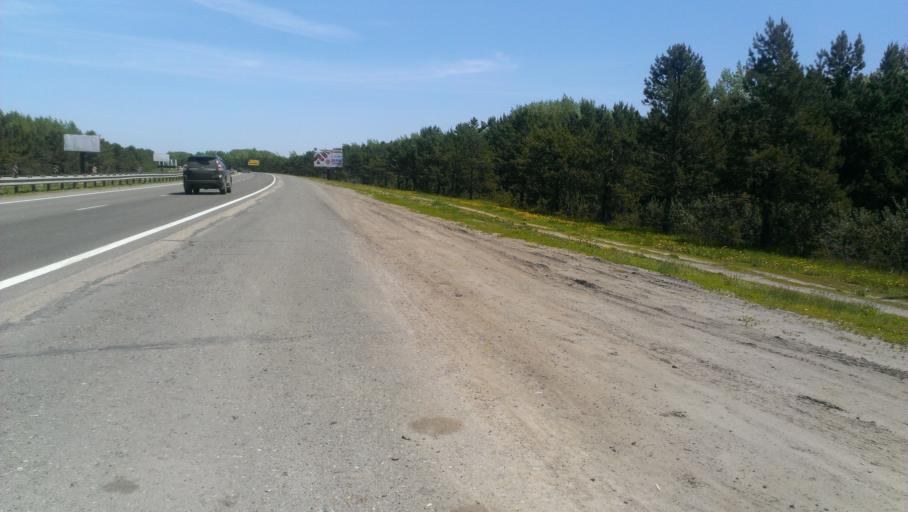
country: RU
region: Altai Krai
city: Zaton
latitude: 53.3149
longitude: 83.8559
